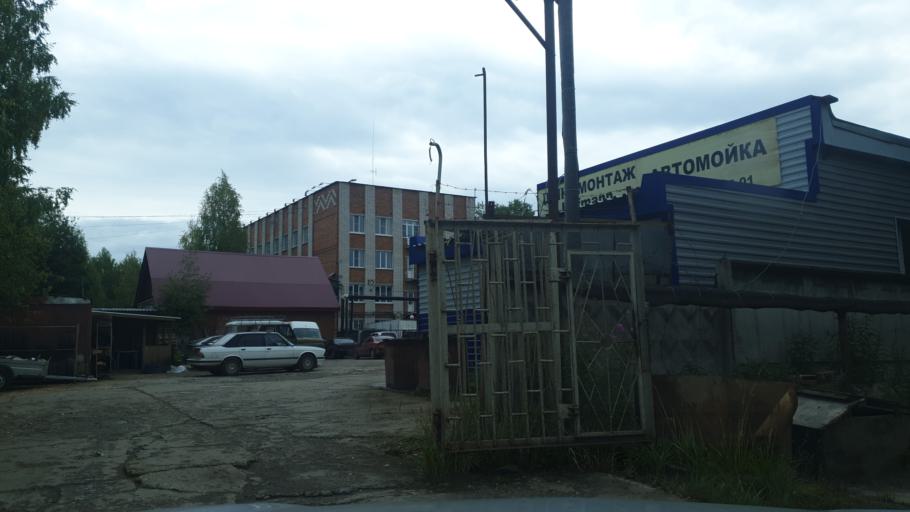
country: RU
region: Komi Republic
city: Ezhva
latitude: 61.8089
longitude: 50.7339
